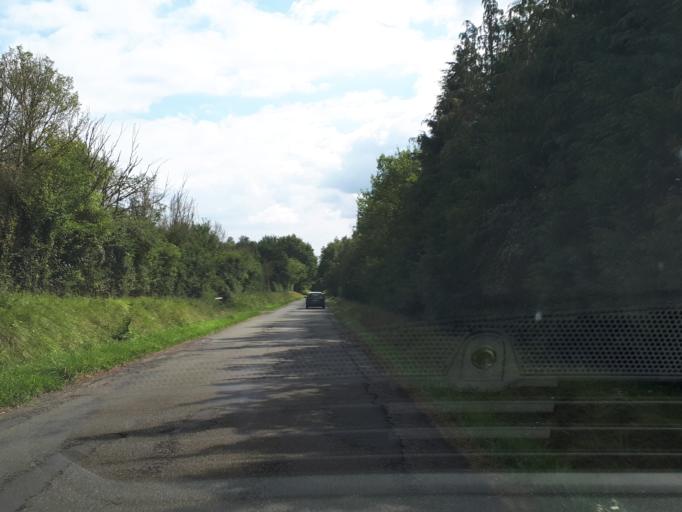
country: FR
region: Pays de la Loire
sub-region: Departement de la Sarthe
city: Champagne
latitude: 48.0571
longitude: 0.3086
